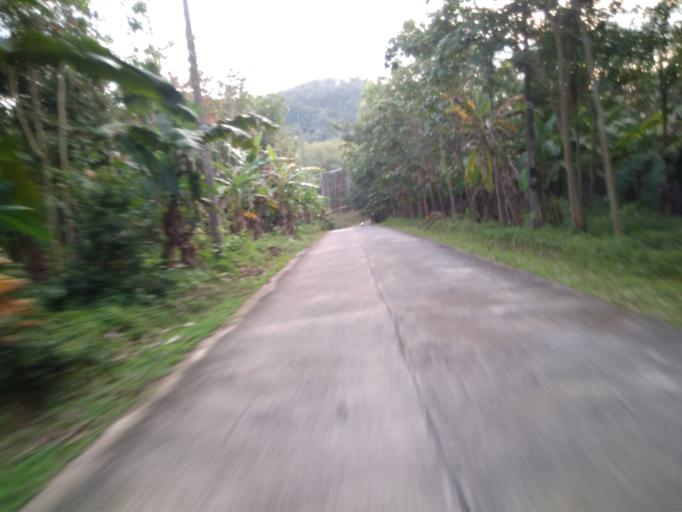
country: TH
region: Phangnga
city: Ko Yao
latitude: 8.1589
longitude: 98.6083
